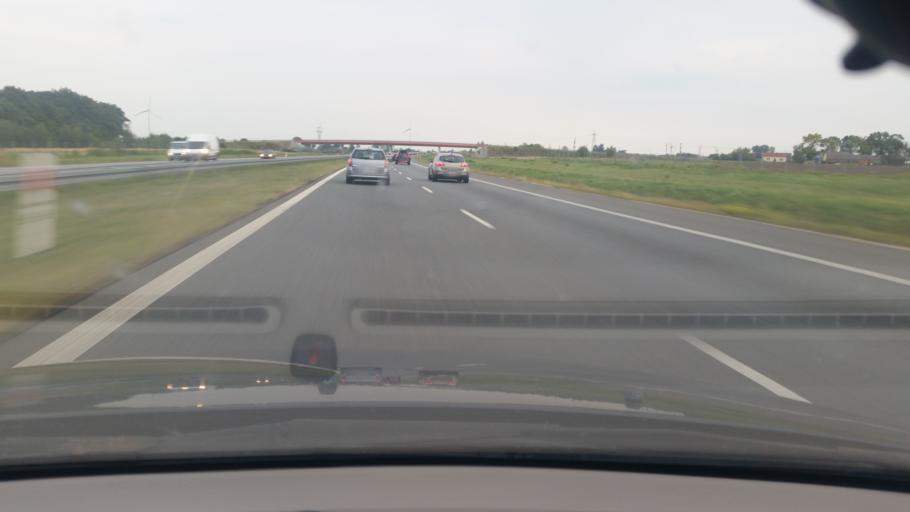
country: PL
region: Lodz Voivodeship
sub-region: Powiat kutnowski
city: Strzelce
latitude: 52.2574
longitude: 19.4398
